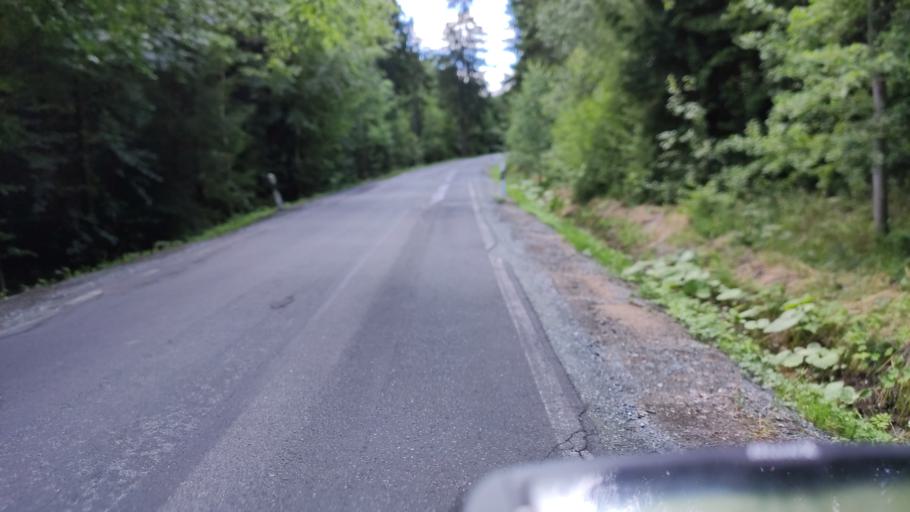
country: DE
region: Thuringia
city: Bad Lobenstein
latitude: 50.4835
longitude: 11.5989
